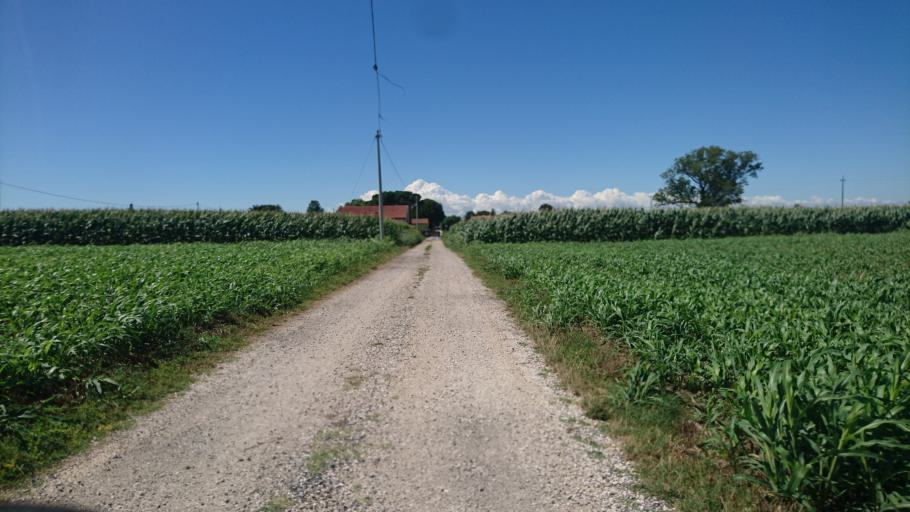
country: IT
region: Veneto
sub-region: Provincia di Padova
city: Pontelongo
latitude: 45.2564
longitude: 12.0191
